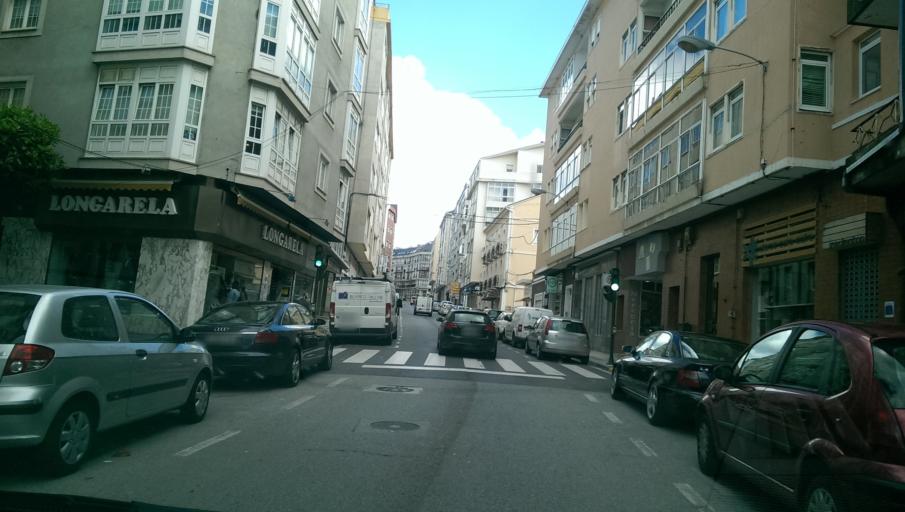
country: ES
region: Galicia
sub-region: Provincia de Lugo
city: Foz
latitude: 43.5676
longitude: -7.2589
